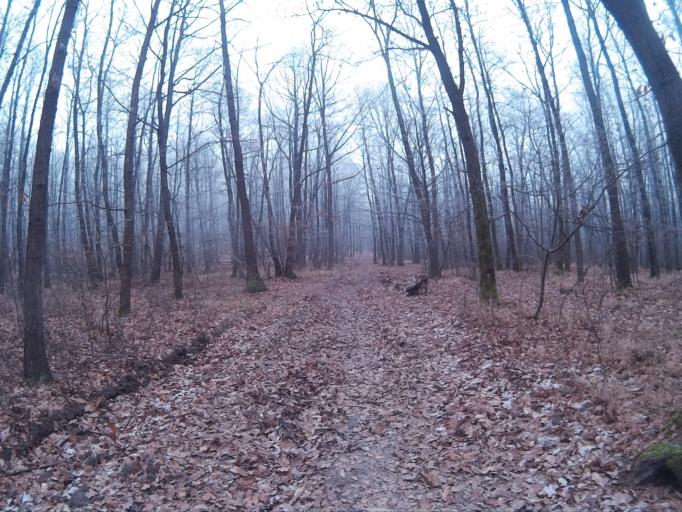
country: HU
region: Nograd
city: Rimoc
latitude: 47.9796
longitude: 19.5575
